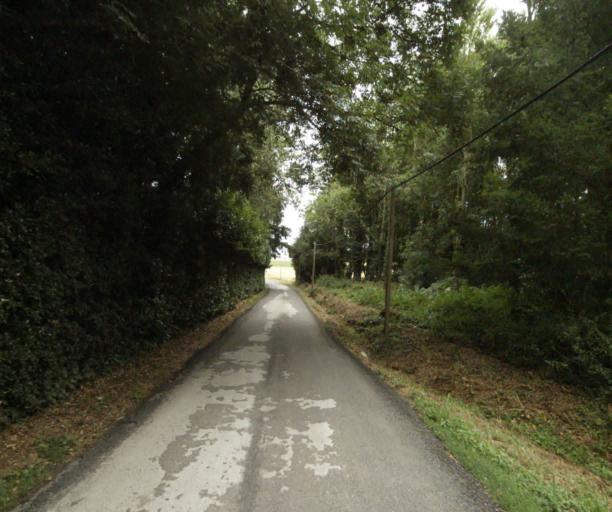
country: FR
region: Midi-Pyrenees
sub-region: Departement du Tarn
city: Soreze
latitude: 43.4064
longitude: 2.0718
